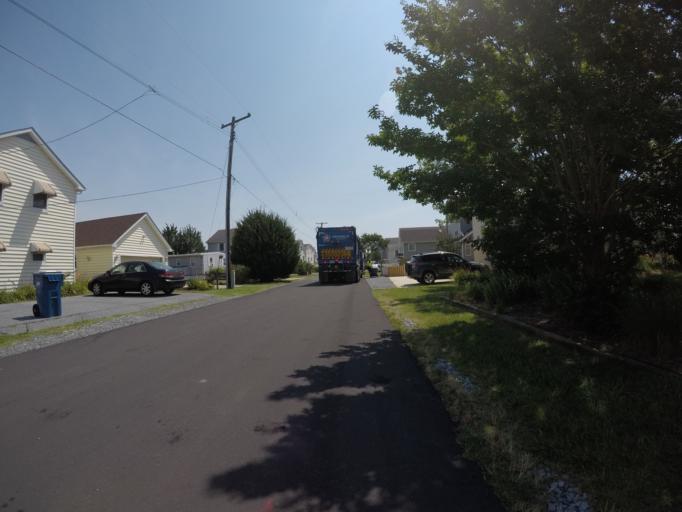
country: US
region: Delaware
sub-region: Sussex County
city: Bethany Beach
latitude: 38.5167
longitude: -75.0601
